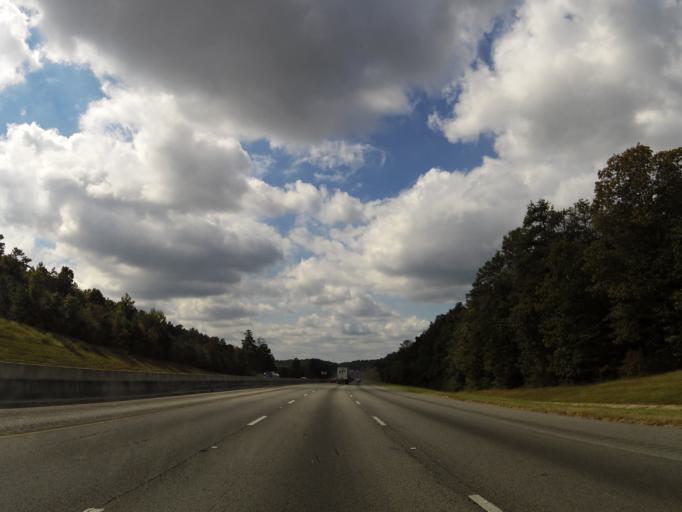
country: US
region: Alabama
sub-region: Tuscaloosa County
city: Lake View
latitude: 33.3143
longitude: -87.0571
